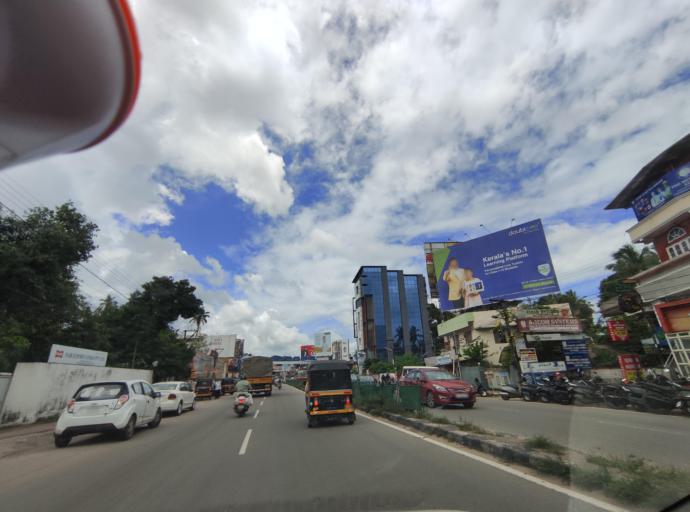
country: IN
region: Kerala
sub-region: Thiruvananthapuram
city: Thiruvananthapuram
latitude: 8.5165
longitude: 76.9443
